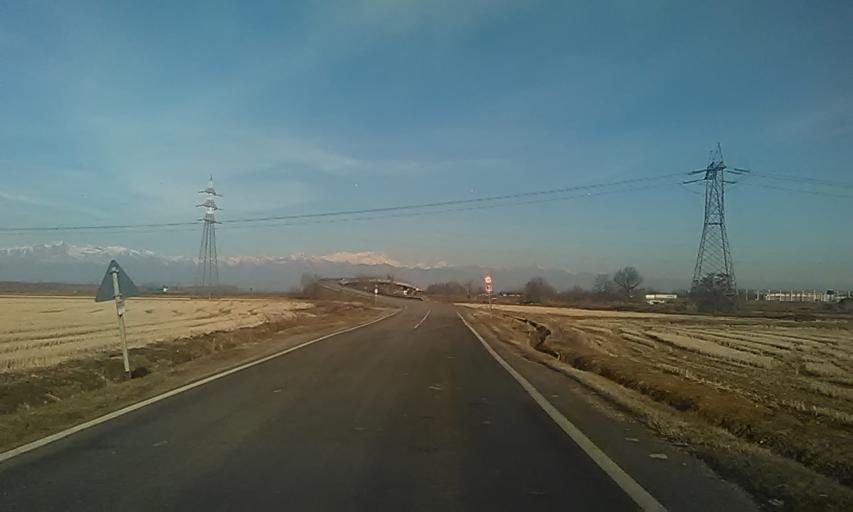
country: IT
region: Piedmont
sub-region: Provincia di Vercelli
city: Formigliana
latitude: 45.4428
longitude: 8.2893
